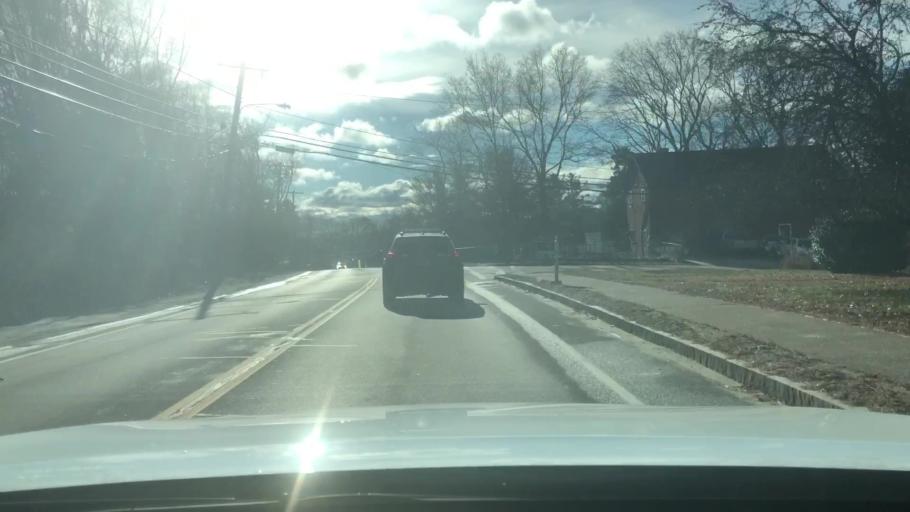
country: US
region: Massachusetts
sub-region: Norfolk County
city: Bellingham
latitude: 42.0557
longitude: -71.4850
